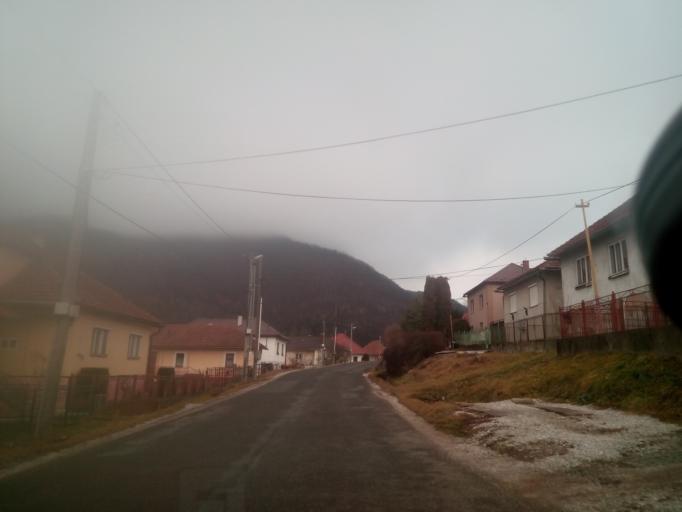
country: SK
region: Kosicky
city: Krompachy
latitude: 48.9357
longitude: 20.9405
